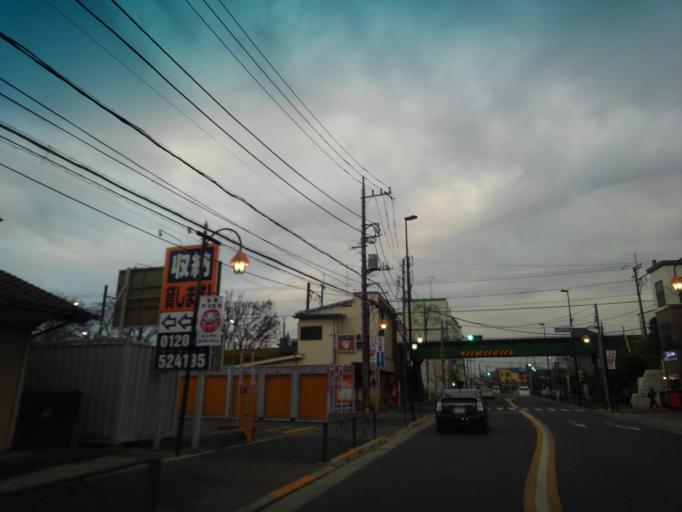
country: JP
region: Tokyo
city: Higashimurayama-shi
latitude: 35.7560
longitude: 139.4450
